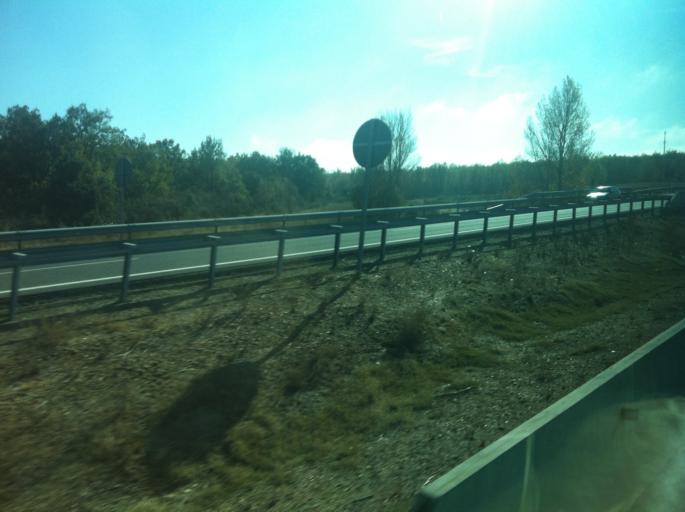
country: ES
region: Castille and Leon
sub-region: Provincia de Burgos
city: Madrigalejo del Monte
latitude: 42.0984
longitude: -3.7240
